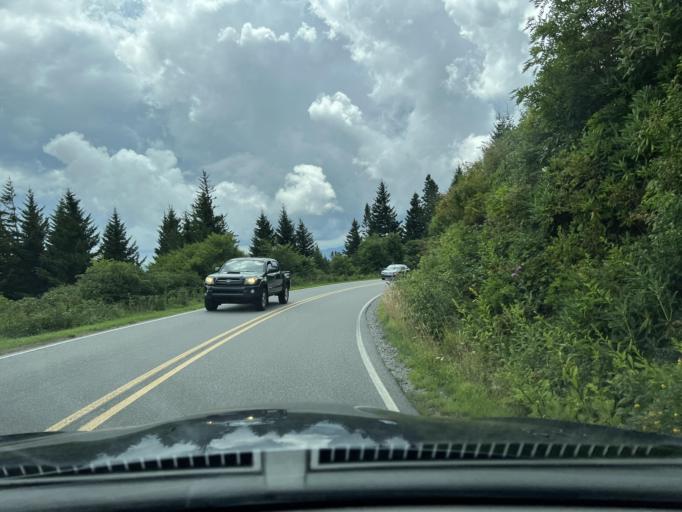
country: US
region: North Carolina
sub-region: Buncombe County
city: Black Mountain
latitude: 35.7300
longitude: -82.2794
